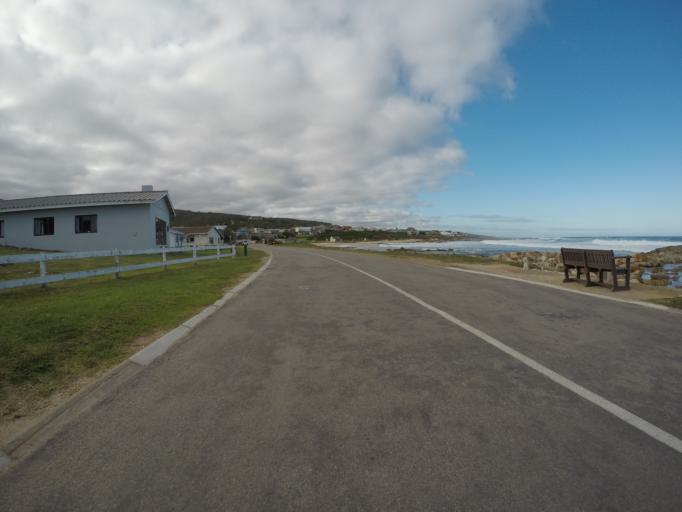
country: ZA
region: Western Cape
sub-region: Eden District Municipality
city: Riversdale
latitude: -34.4277
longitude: 21.3372
